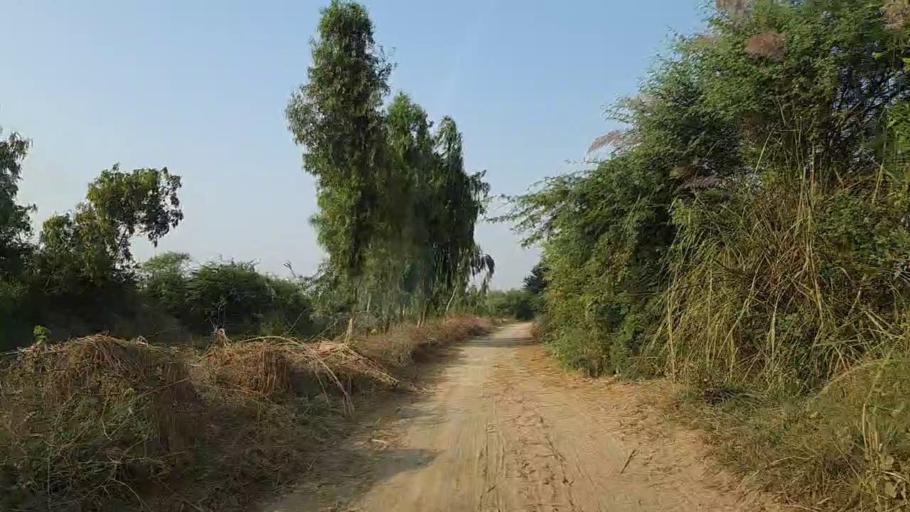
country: PK
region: Sindh
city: Mirpur Sakro
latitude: 24.6513
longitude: 67.7673
